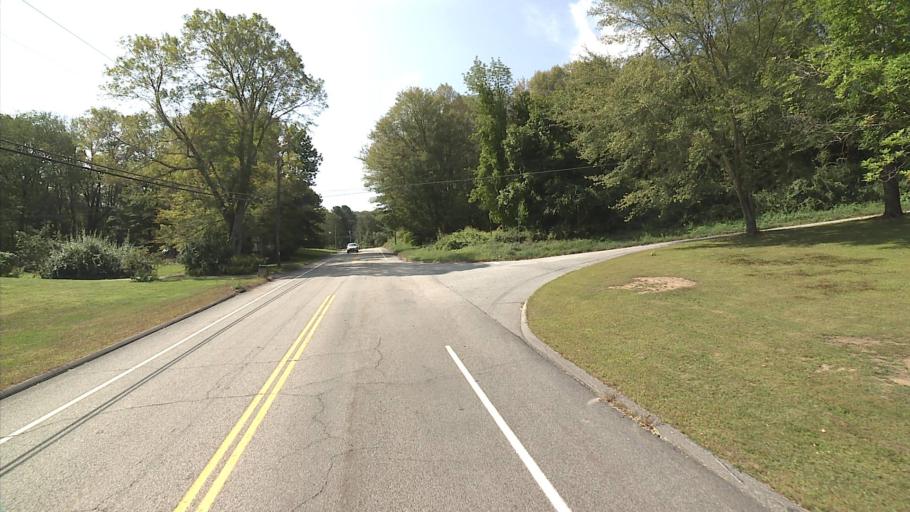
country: US
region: Connecticut
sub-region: Windham County
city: Wauregan
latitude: 41.7380
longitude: -71.9636
